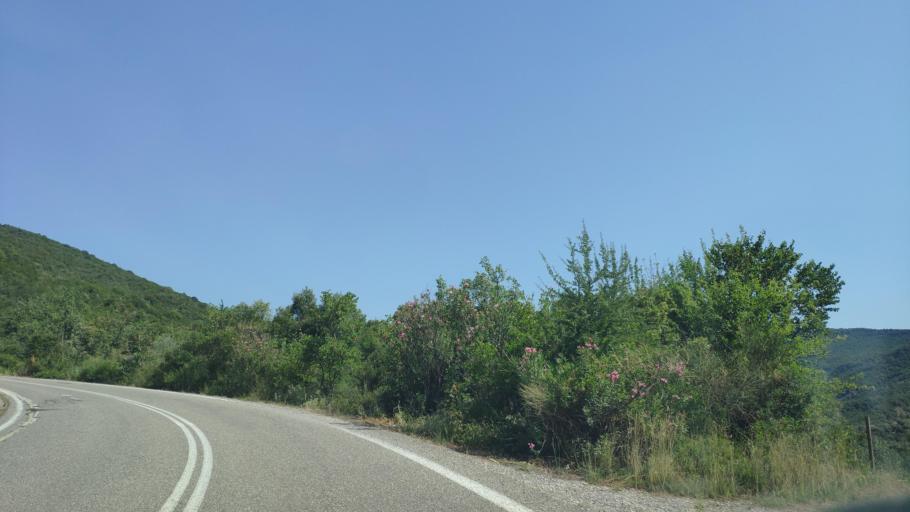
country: GR
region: West Greece
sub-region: Nomos Aitolias kai Akarnanias
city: Lepenou
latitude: 38.7600
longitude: 21.3388
